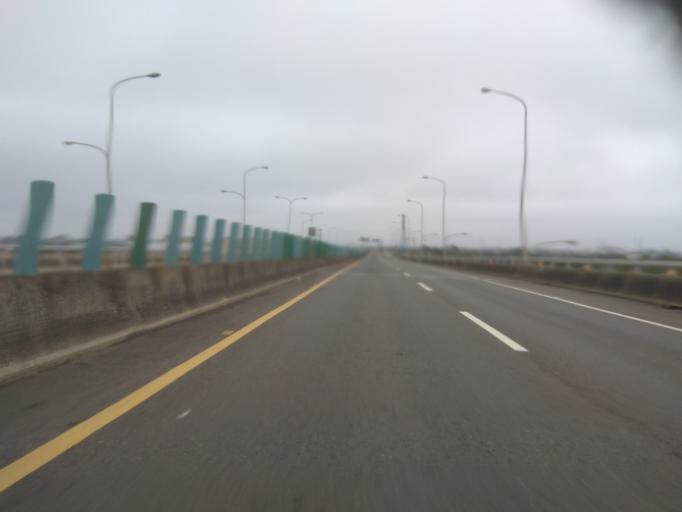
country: TW
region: Taiwan
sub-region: Hsinchu
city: Zhubei
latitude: 24.9999
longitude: 121.1010
